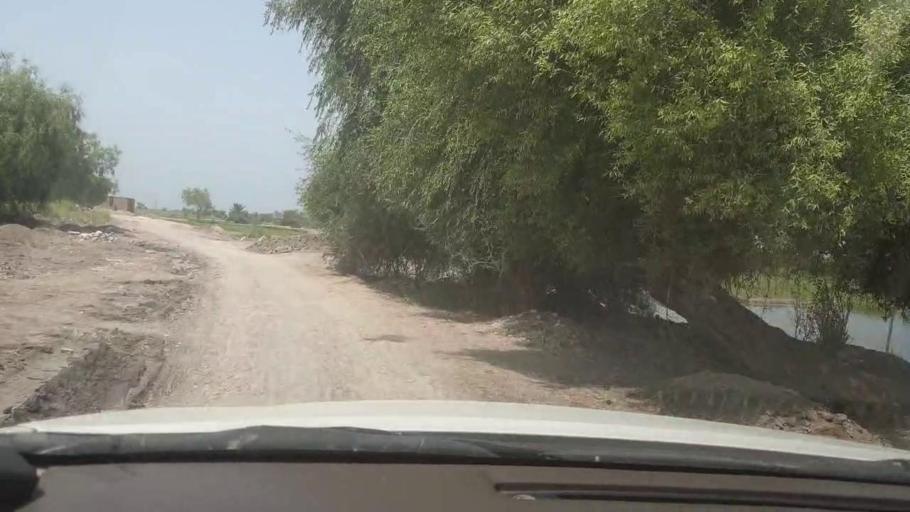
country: PK
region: Sindh
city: Shikarpur
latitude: 27.9570
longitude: 68.5941
